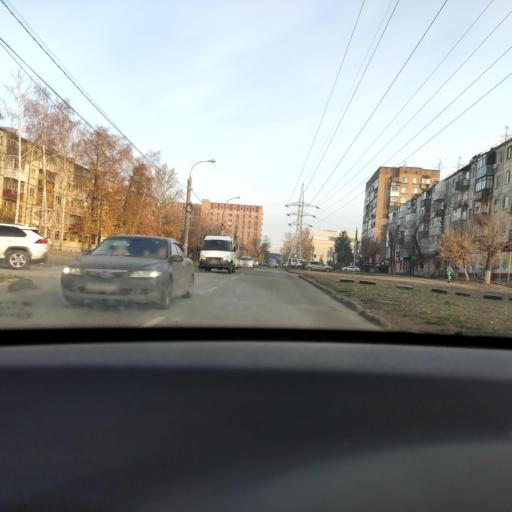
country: RU
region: Samara
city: Samara
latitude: 53.1982
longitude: 50.1712
